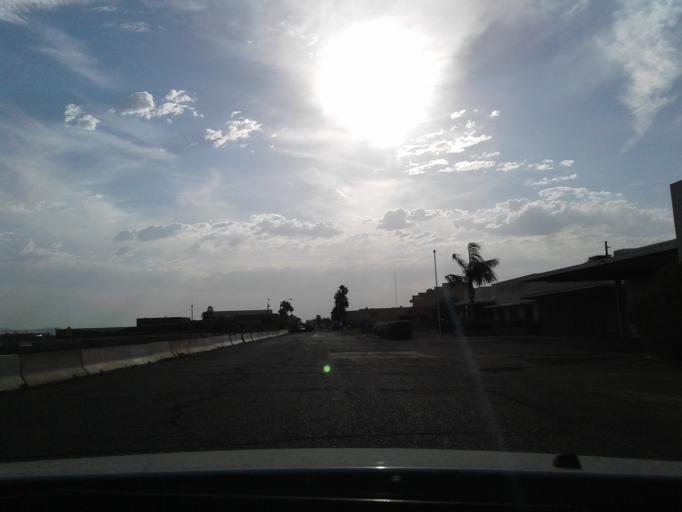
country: US
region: Arizona
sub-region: Maricopa County
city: Tempe Junction
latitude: 33.4431
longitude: -111.9936
